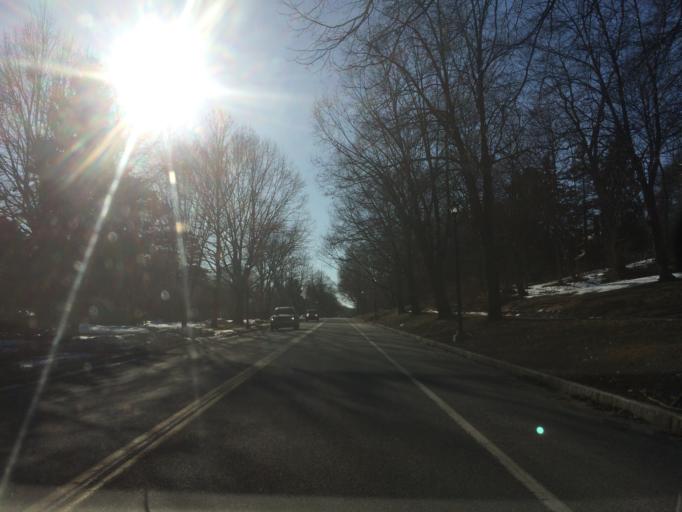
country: US
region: New York
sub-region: Monroe County
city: Brighton
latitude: 43.1364
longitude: -77.5687
